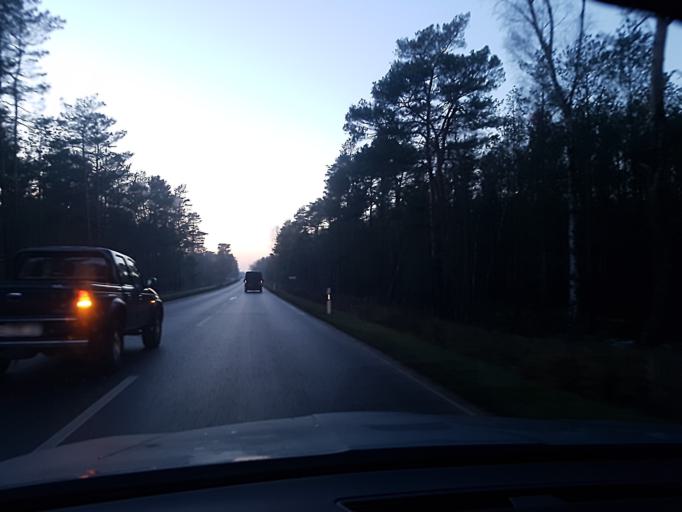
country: DE
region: Brandenburg
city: Sonnewalde
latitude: 51.6346
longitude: 13.6407
